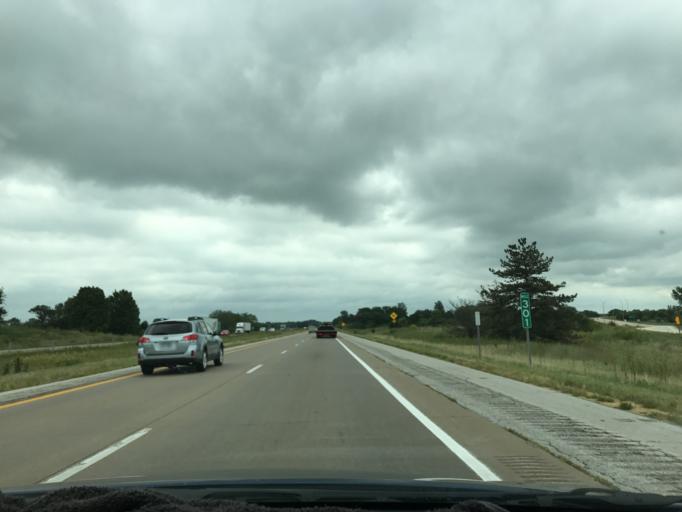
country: US
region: Illinois
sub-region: Rock Island County
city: Hampton
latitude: 41.5969
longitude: -90.4660
